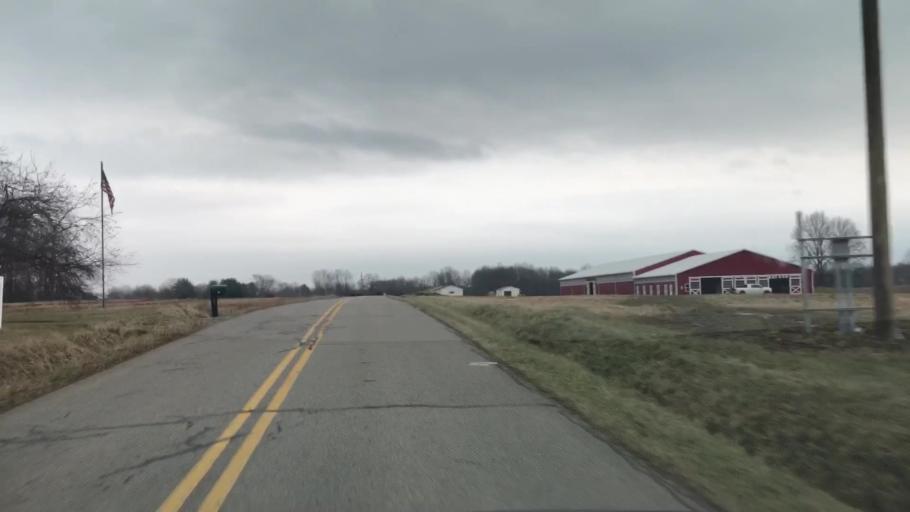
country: US
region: Pennsylvania
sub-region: Mercer County
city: Grove City
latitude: 41.1338
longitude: -80.1266
